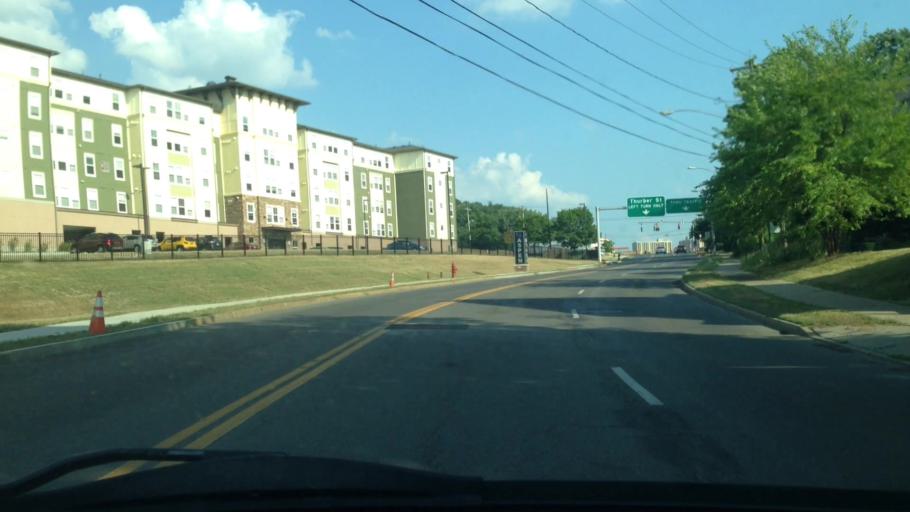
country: US
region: New York
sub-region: Onondaga County
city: Syracuse
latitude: 43.0193
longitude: -76.1390
